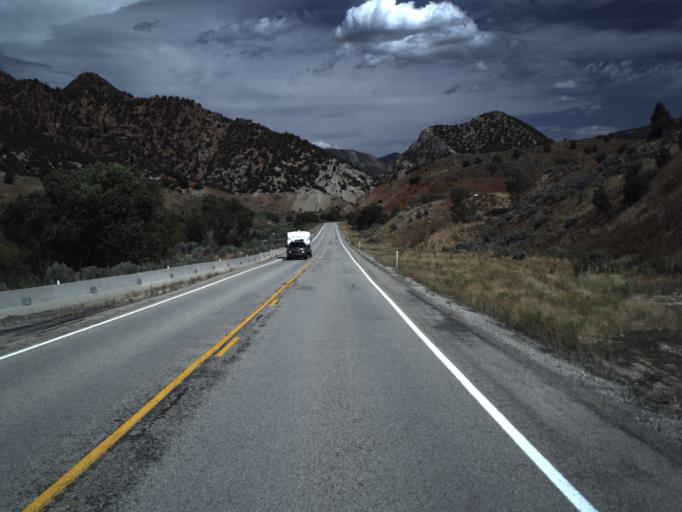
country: US
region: Utah
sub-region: Utah County
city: Woodland Hills
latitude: 39.9776
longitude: -111.5034
